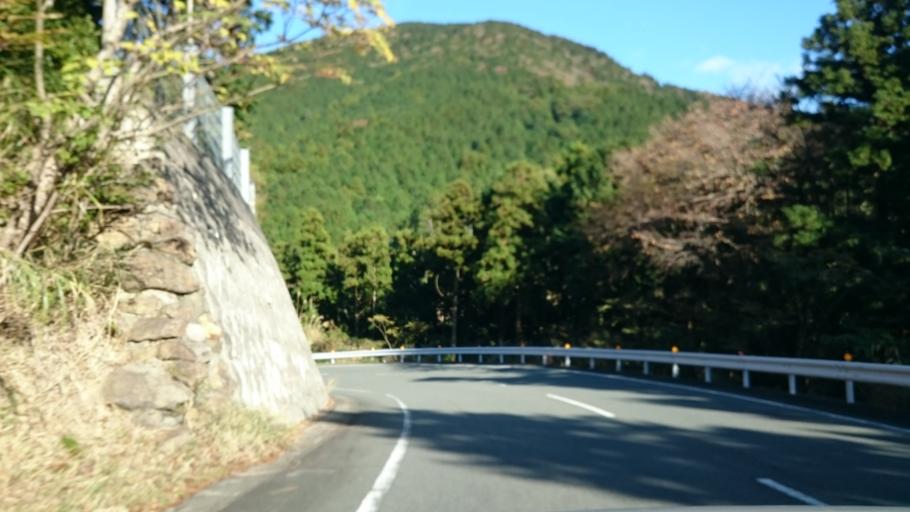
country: JP
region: Shizuoka
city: Heda
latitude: 34.9789
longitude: 138.8146
